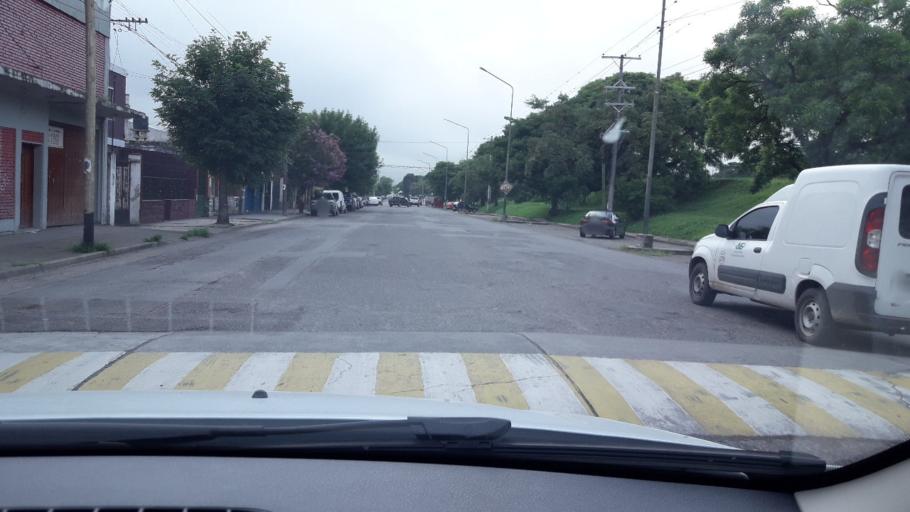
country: AR
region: Jujuy
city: San Salvador de Jujuy
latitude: -24.1949
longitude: -65.2916
